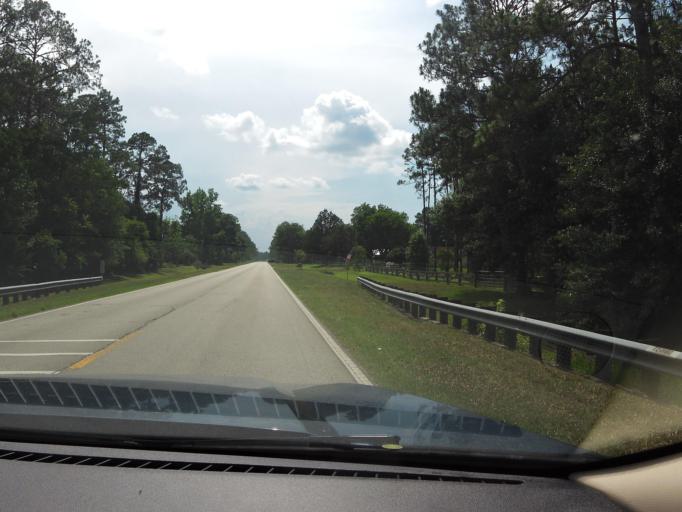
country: US
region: Florida
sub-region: Duval County
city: Baldwin
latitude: 30.2020
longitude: -82.0175
